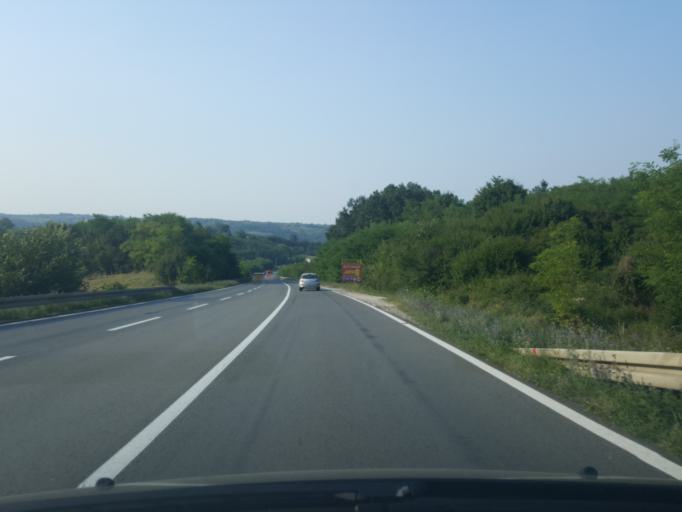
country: RS
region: Central Serbia
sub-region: Belgrade
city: Sopot
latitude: 44.5546
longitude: 20.6667
